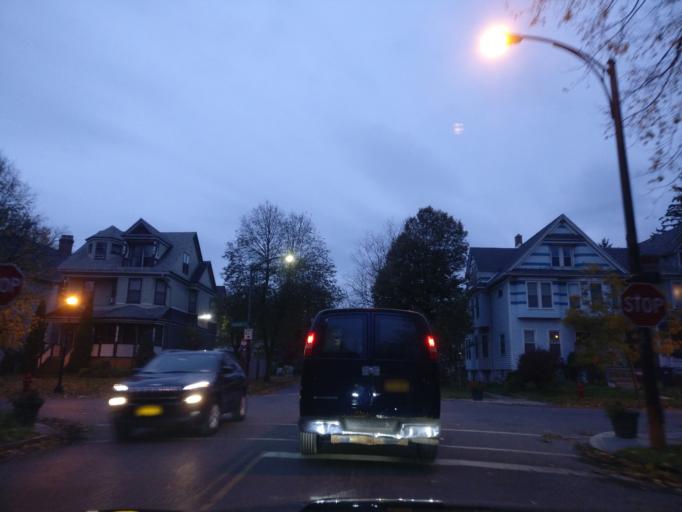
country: US
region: New York
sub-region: Erie County
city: Buffalo
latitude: 42.9113
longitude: -78.8784
